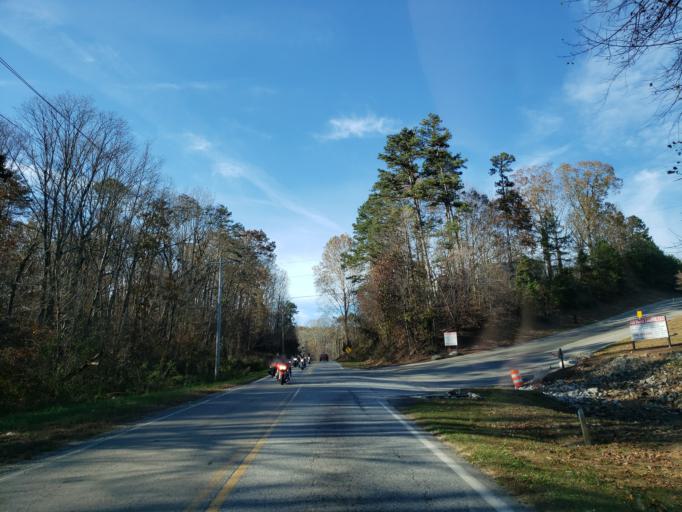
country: US
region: Georgia
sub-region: Lumpkin County
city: Dahlonega
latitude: 34.4506
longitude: -83.9924
